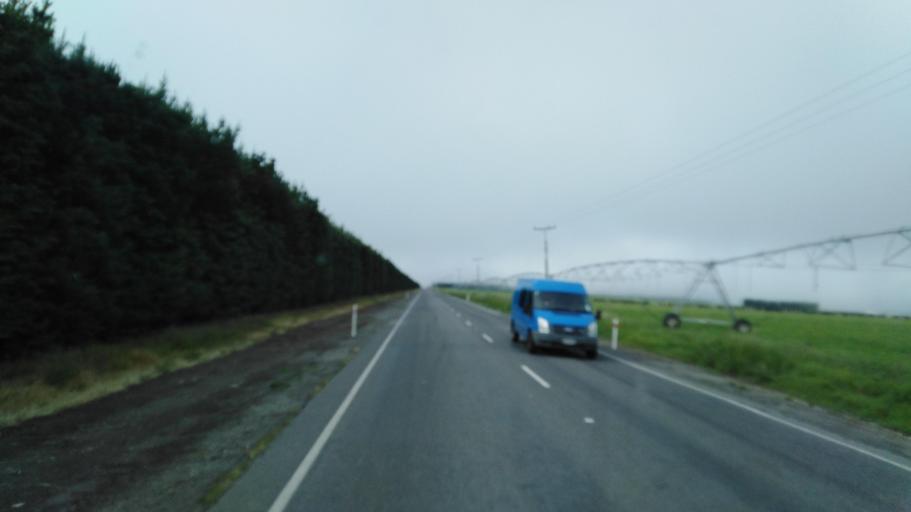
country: NZ
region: Canterbury
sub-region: Hurunui District
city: Amberley
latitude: -42.8031
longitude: 172.8249
